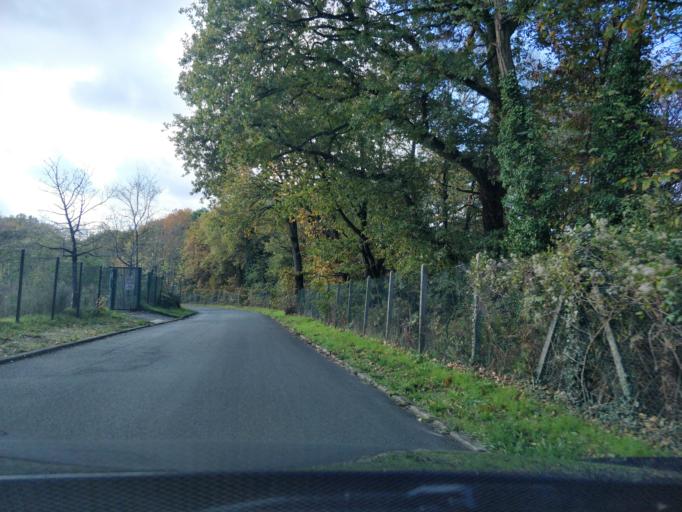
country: FR
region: Ile-de-France
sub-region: Departement de l'Essonne
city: Briis-sous-Forges
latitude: 48.6275
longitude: 2.1332
